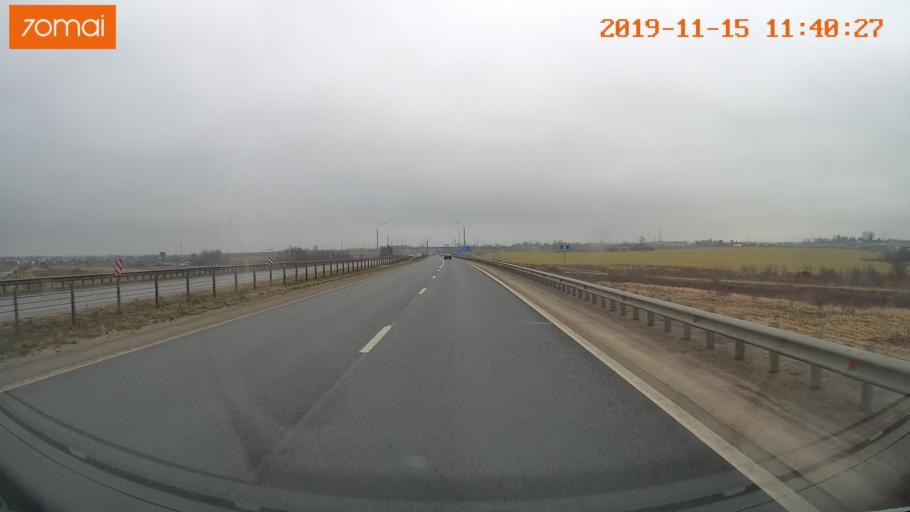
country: RU
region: Vologda
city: Molochnoye
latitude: 59.2125
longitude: 39.7517
